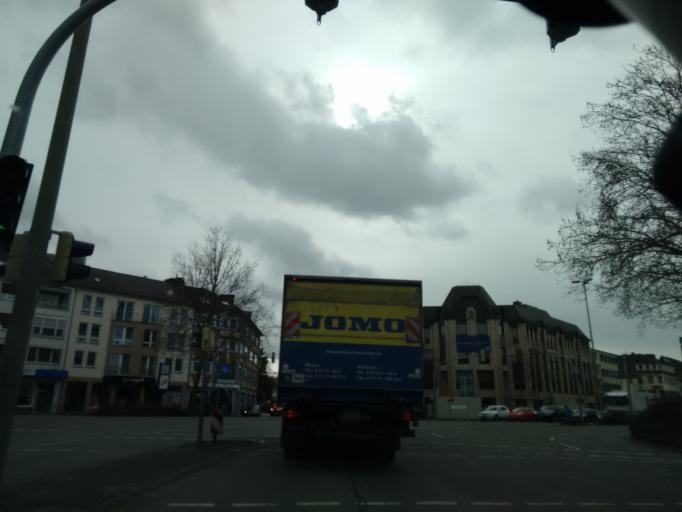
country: DE
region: North Rhine-Westphalia
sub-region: Regierungsbezirk Detmold
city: Paderborn
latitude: 51.7157
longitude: 8.7465
